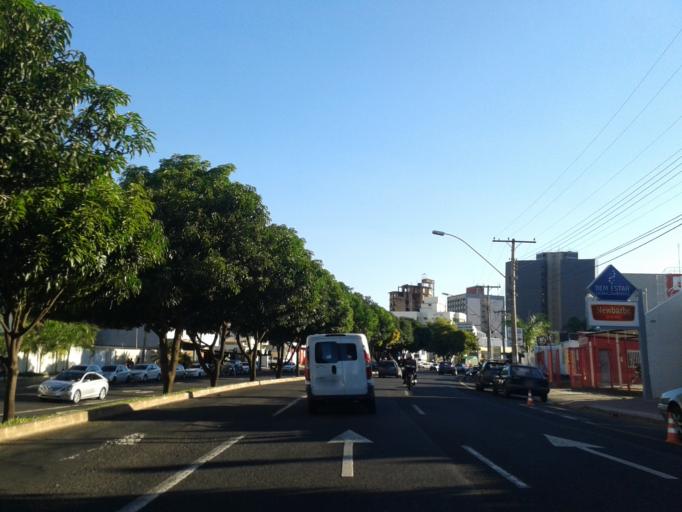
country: BR
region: Minas Gerais
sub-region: Uberlandia
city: Uberlandia
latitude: -18.9155
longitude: -48.2695
